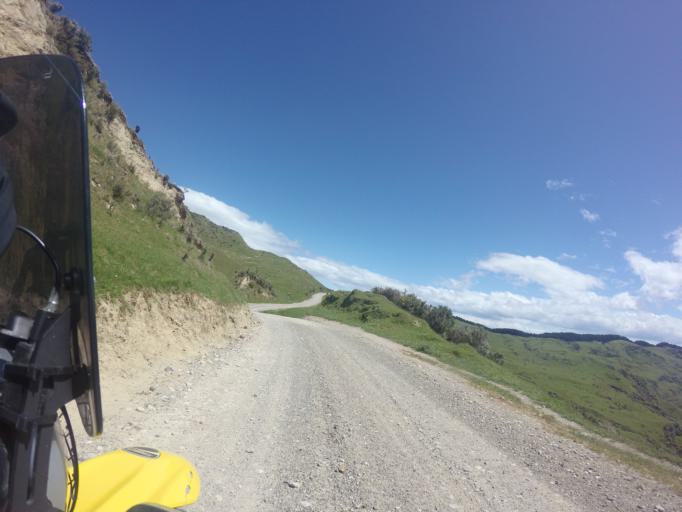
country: NZ
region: Hawke's Bay
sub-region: Wairoa District
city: Wairoa
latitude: -38.9511
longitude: 177.7236
